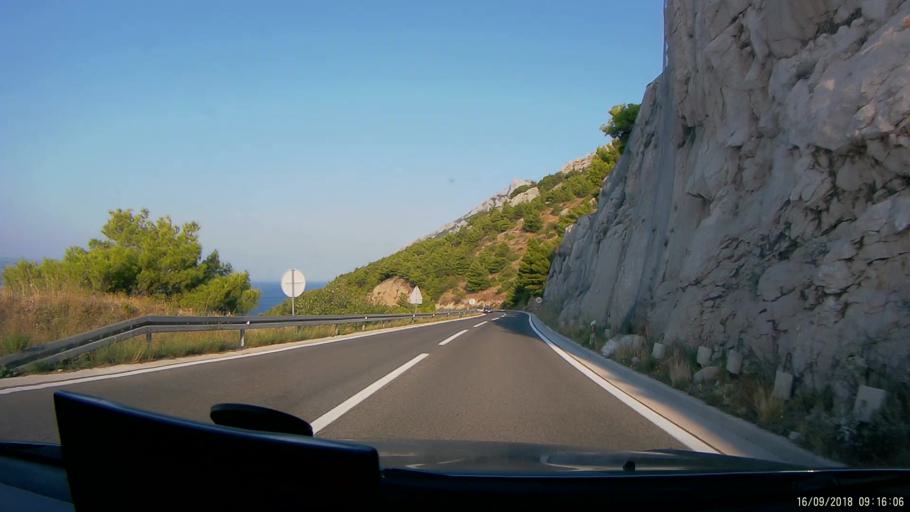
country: HR
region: Splitsko-Dalmatinska
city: Donja Brela
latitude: 43.4003
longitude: 16.8715
